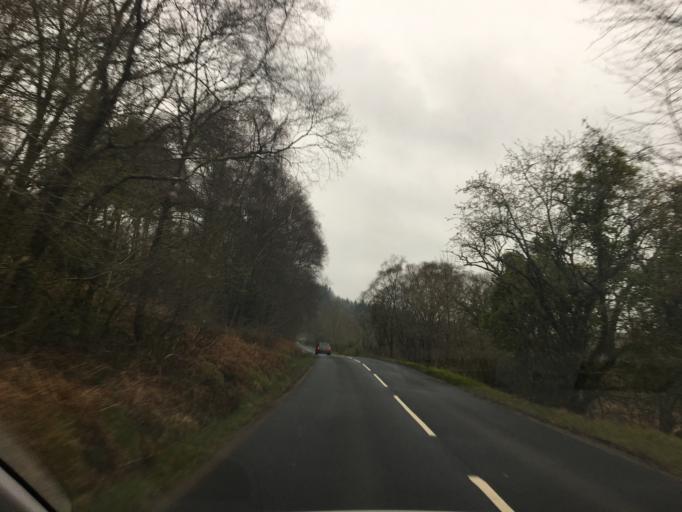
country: GB
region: Scotland
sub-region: North Ayrshire
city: Lamlash
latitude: 55.5487
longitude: -5.1383
